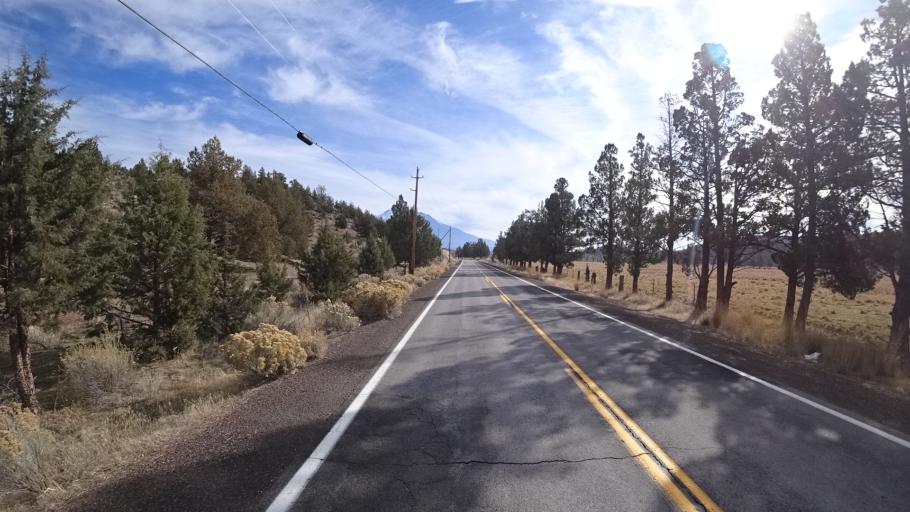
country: US
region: California
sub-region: Siskiyou County
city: Weed
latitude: 41.5765
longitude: -122.3954
